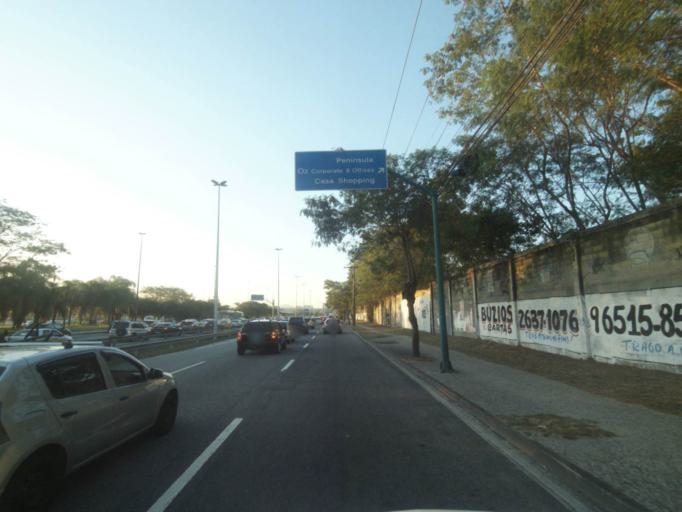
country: BR
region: Rio de Janeiro
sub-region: Rio De Janeiro
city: Rio de Janeiro
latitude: -22.9870
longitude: -43.3654
